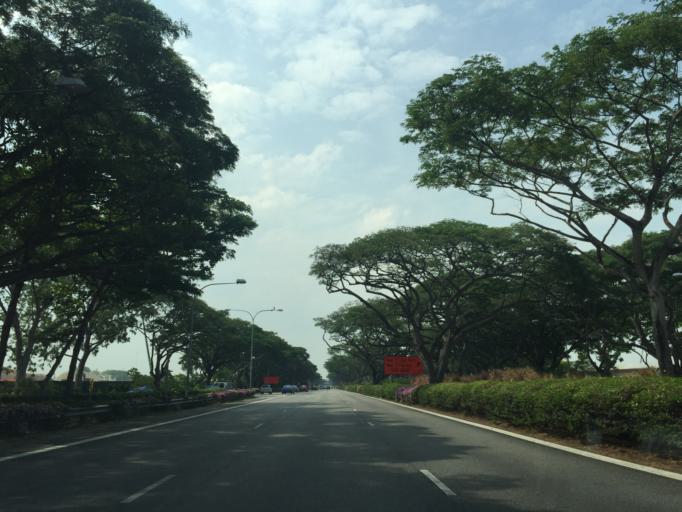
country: SG
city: Singapore
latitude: 1.3377
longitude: 103.9801
